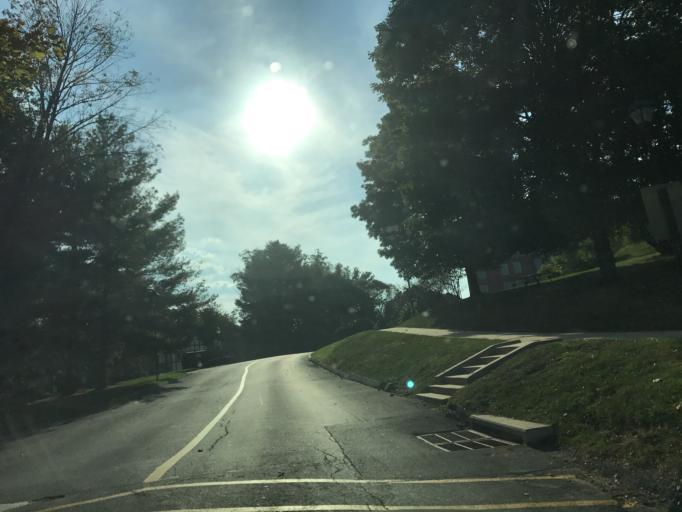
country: US
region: Maryland
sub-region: Baltimore County
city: Towson
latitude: 39.3905
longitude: -76.6175
